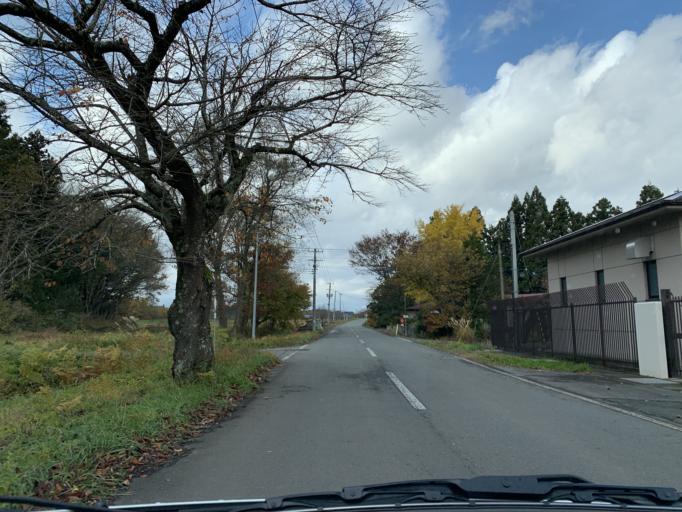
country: JP
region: Iwate
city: Mizusawa
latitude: 39.0656
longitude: 141.0810
